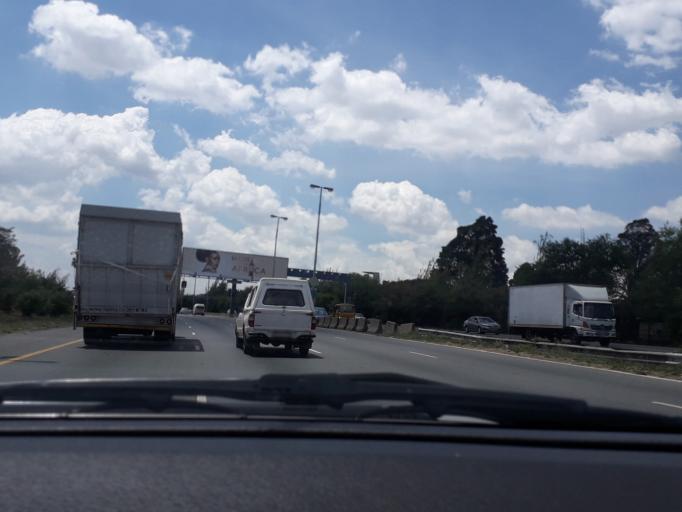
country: ZA
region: Gauteng
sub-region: City of Johannesburg Metropolitan Municipality
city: Johannesburg
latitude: -26.2505
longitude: 27.9979
